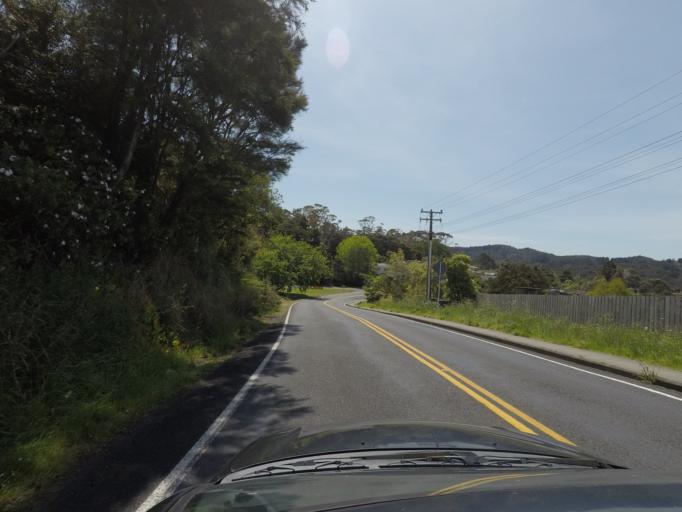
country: NZ
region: Auckland
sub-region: Auckland
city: Titirangi
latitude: -36.9738
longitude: 174.6146
